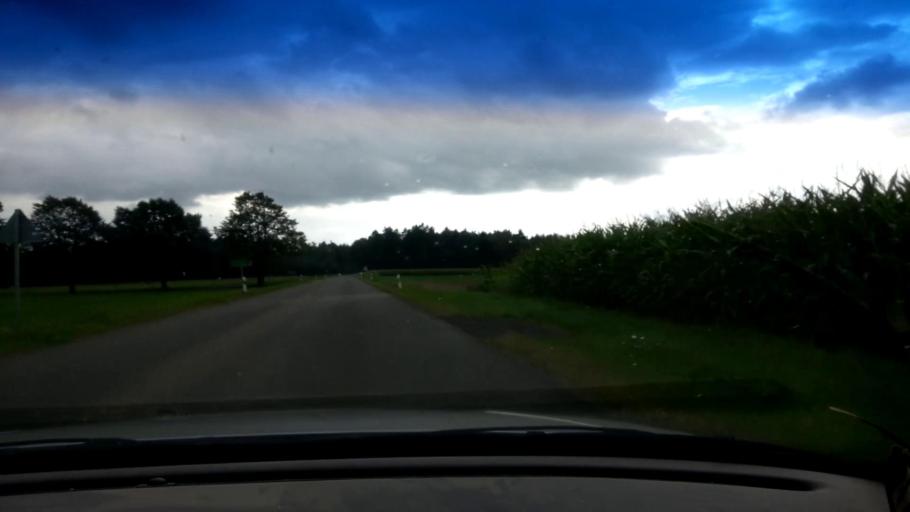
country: DE
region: Bavaria
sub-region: Upper Palatinate
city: Waldsassen
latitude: 50.0302
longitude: 12.2768
